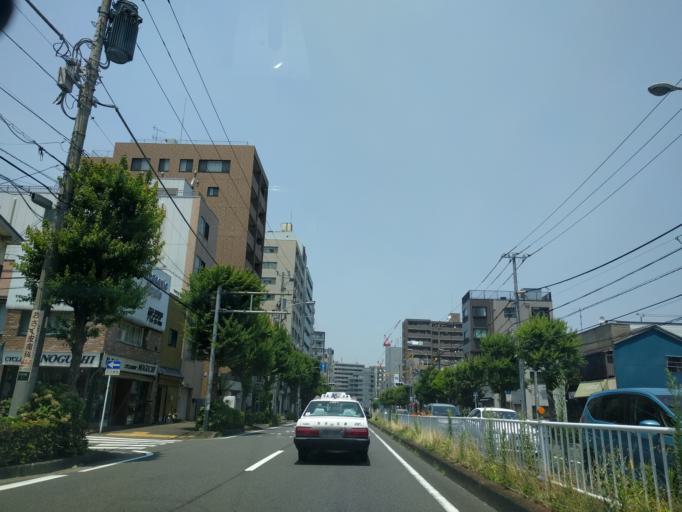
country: JP
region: Kanagawa
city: Yokohama
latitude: 35.4515
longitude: 139.6131
